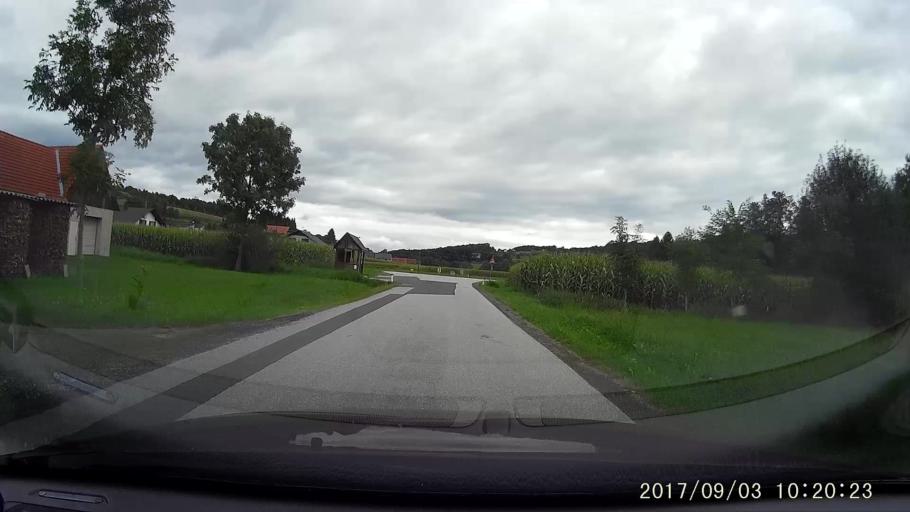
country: AT
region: Styria
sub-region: Politischer Bezirk Suedoststeiermark
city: Breitenfeld an der Rittschein
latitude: 47.0352
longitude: 15.9115
